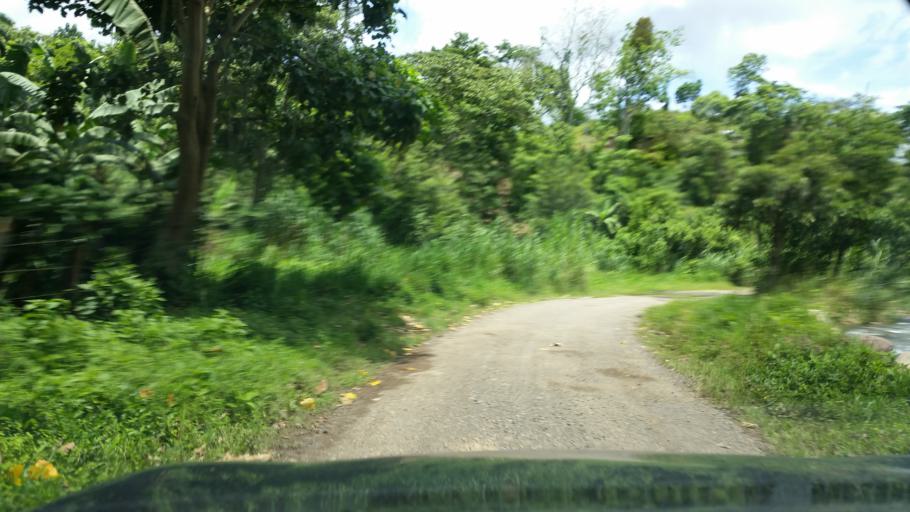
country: NI
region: Atlantico Norte (RAAN)
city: Waslala
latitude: 13.2549
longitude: -85.6184
